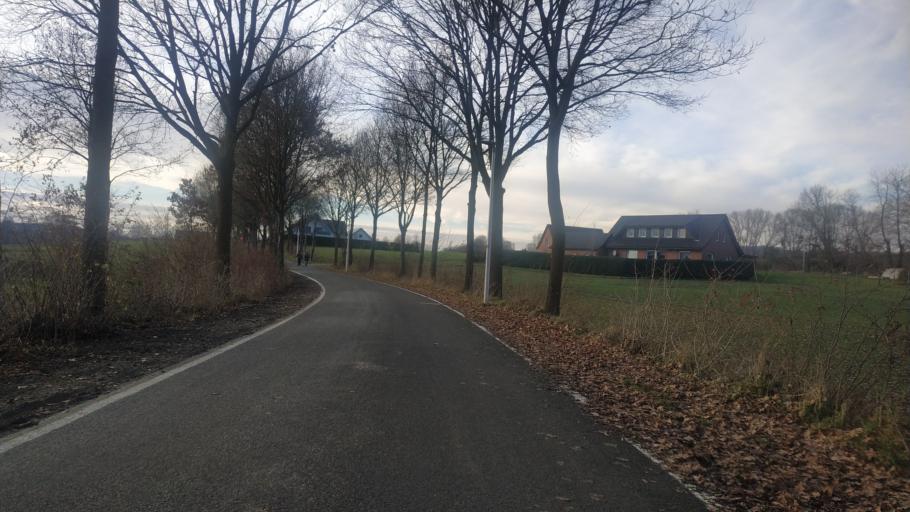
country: DE
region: North Rhine-Westphalia
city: Ibbenburen
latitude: 52.2689
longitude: 7.7622
